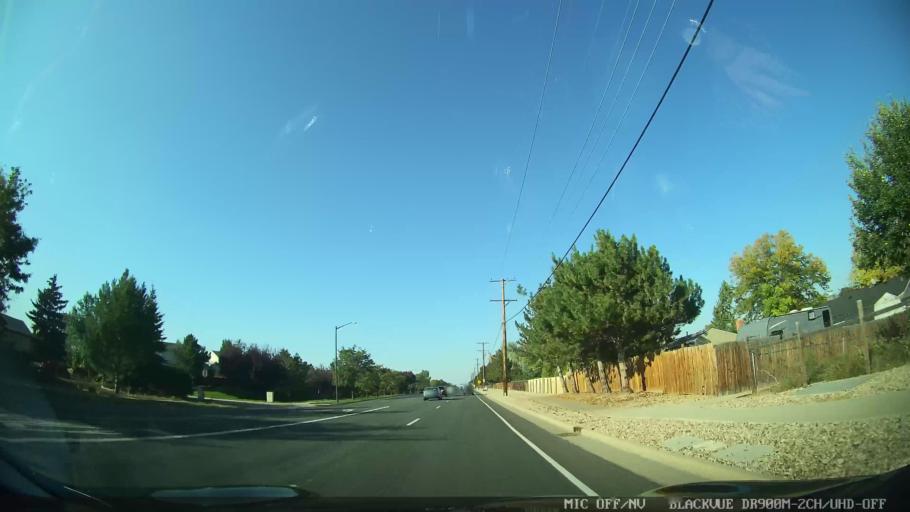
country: US
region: Colorado
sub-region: Larimer County
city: Loveland
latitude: 40.4316
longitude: -105.0965
